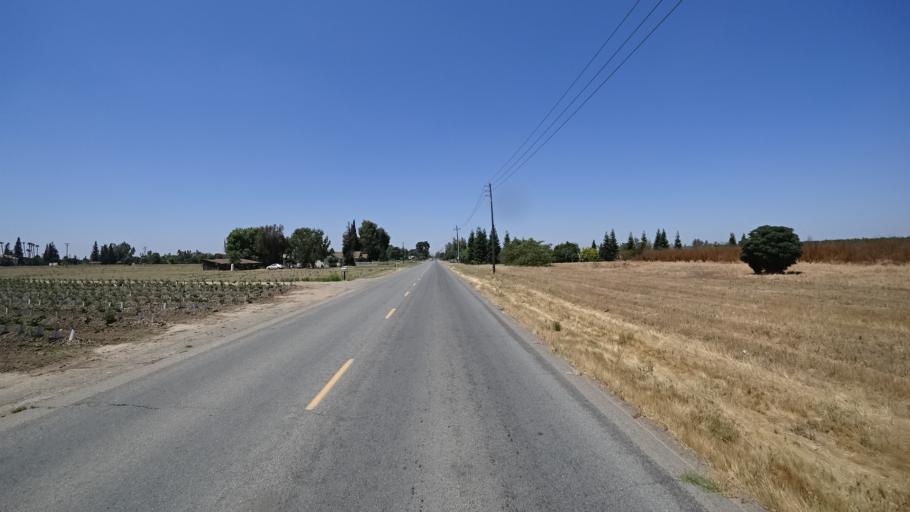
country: US
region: California
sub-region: Fresno County
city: Kingsburg
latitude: 36.4890
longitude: -119.5513
